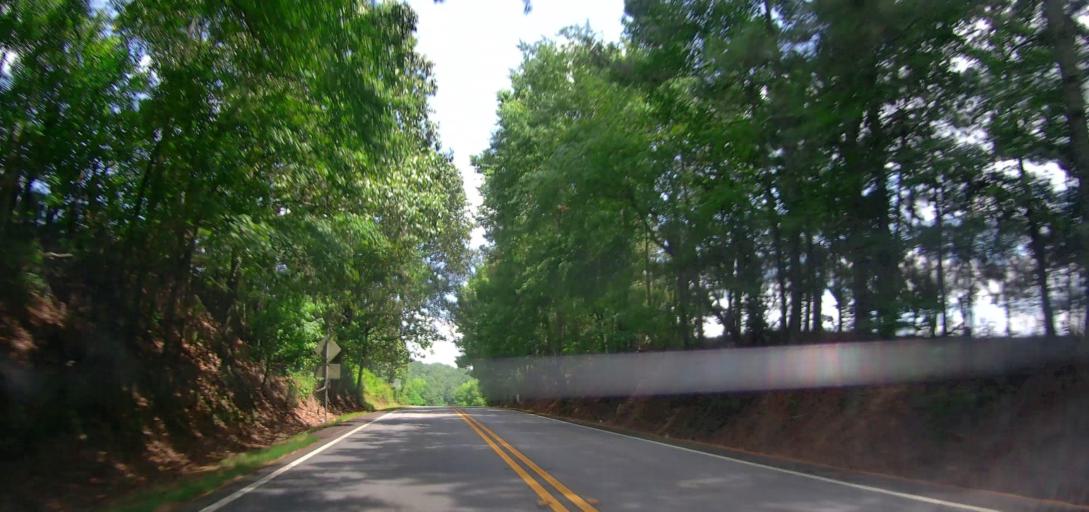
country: US
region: Georgia
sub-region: Carroll County
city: Bowdon
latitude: 33.4356
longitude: -85.2731
